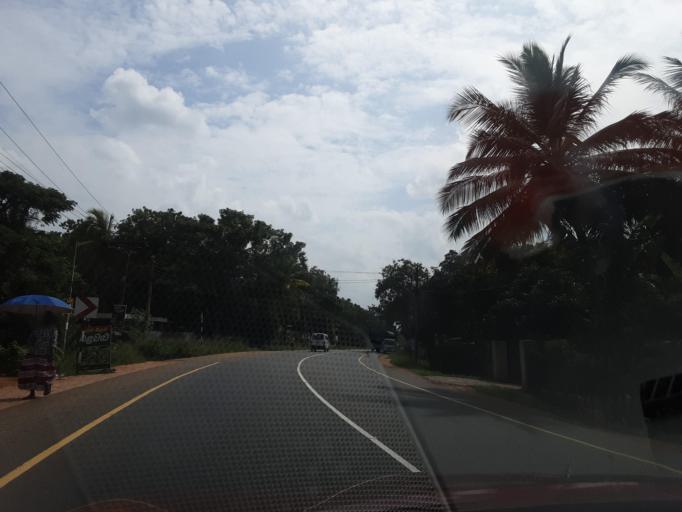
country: LK
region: North Central
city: Anuradhapura
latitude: 8.5019
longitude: 80.5120
